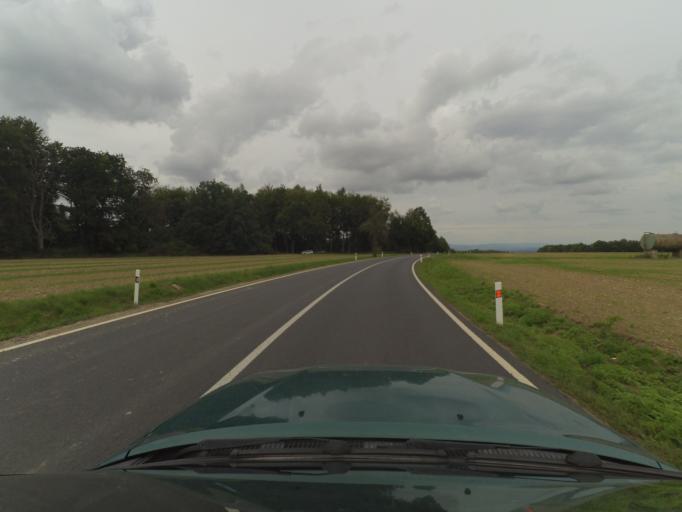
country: CZ
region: Ustecky
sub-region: Okres Louny
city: Louny
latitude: 50.2738
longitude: 13.7736
